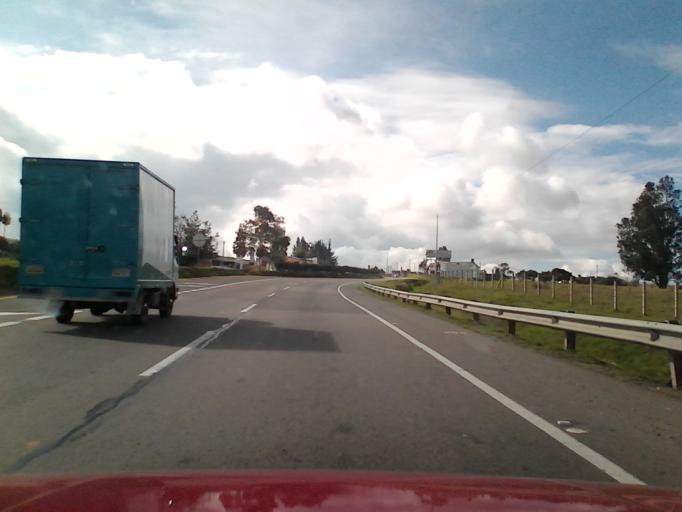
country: CO
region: Boyaca
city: Tuta
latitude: 5.6781
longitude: -73.2696
